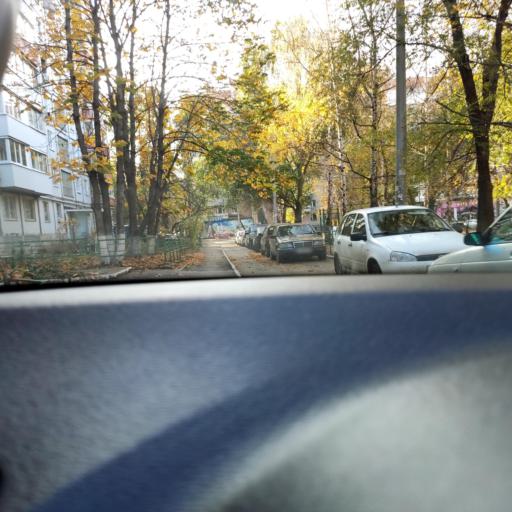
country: RU
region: Samara
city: Samara
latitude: 53.2100
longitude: 50.1428
